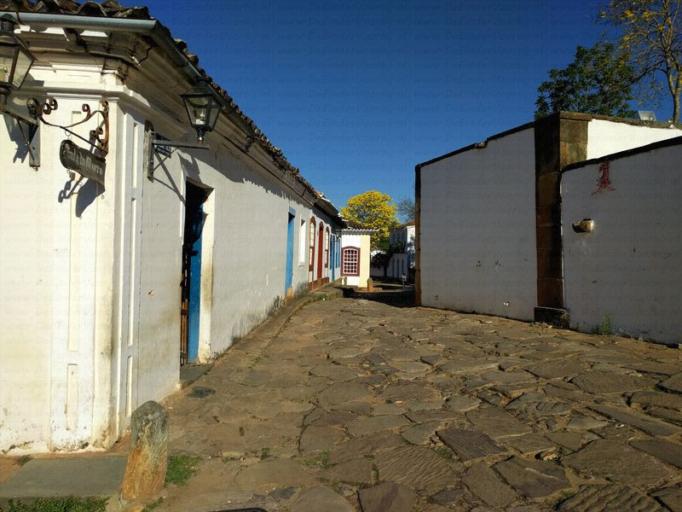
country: BR
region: Minas Gerais
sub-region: Tiradentes
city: Tiradentes
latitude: -21.1100
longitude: -44.1781
